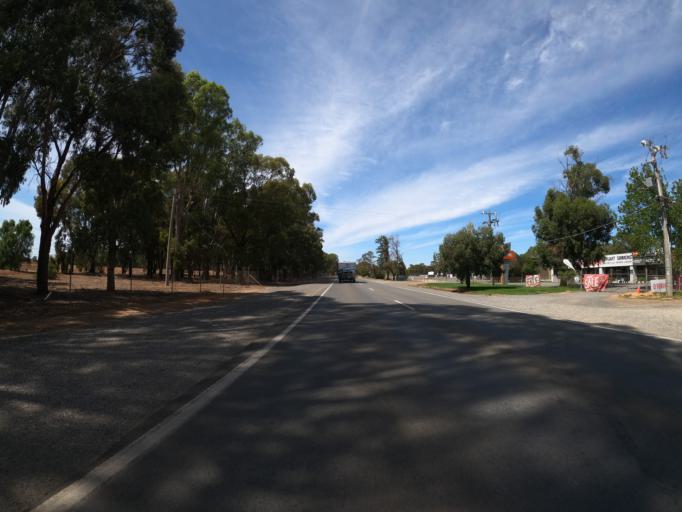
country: AU
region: Victoria
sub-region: Moira
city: Yarrawonga
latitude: -36.0332
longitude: 145.9955
